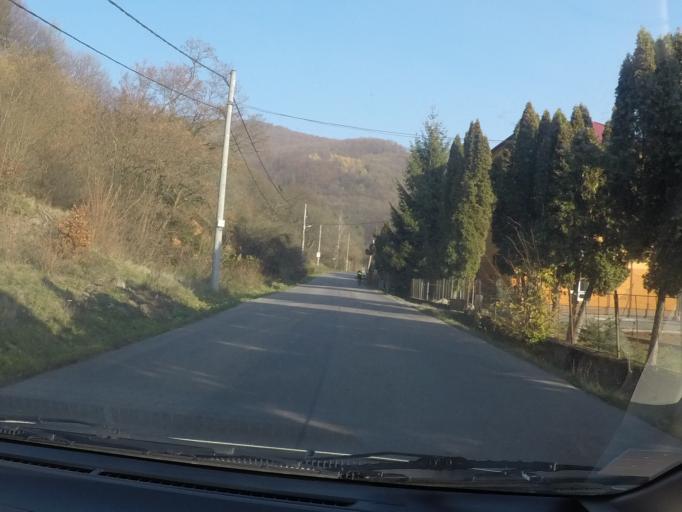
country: SK
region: Banskobystricky
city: Zarnovica
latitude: 48.4609
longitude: 18.7584
